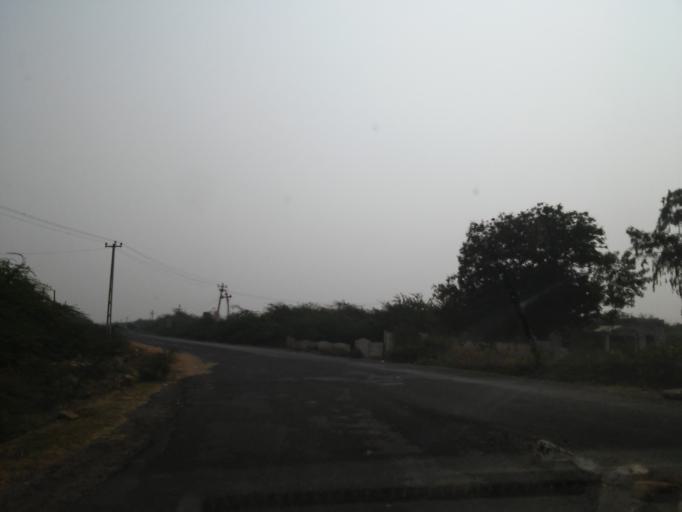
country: IN
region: Gujarat
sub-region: Kachchh
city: Bhuj
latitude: 23.4321
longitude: 69.6618
